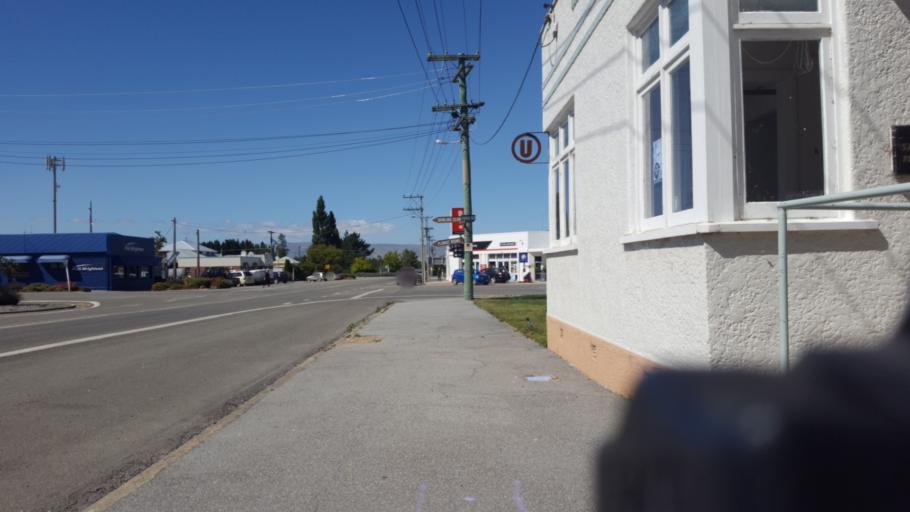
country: NZ
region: Otago
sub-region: Dunedin City
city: Dunedin
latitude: -45.1287
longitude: 170.1004
